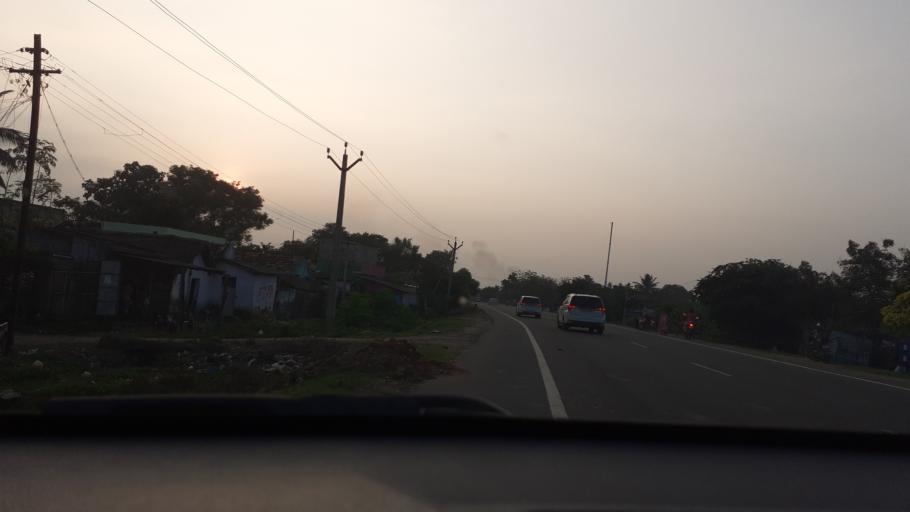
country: IN
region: Tamil Nadu
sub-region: Dindigul
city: Palani
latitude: 10.4320
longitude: 77.5151
